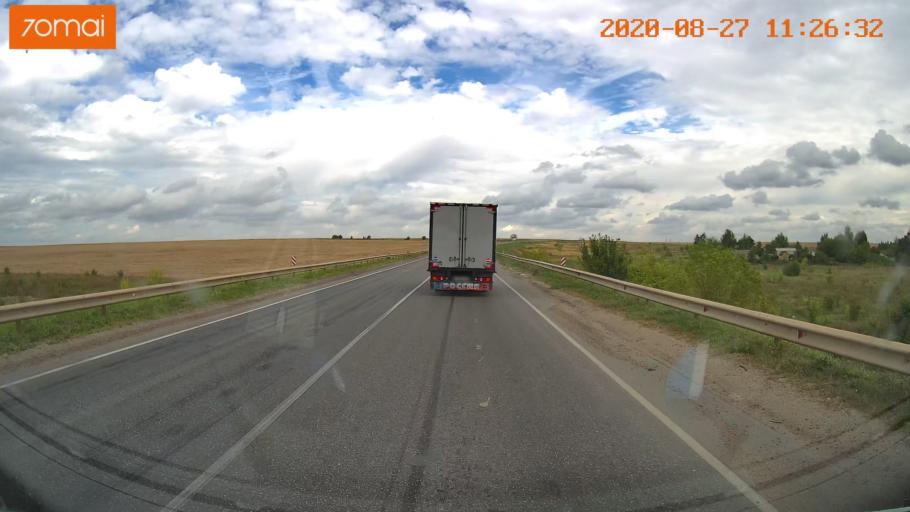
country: RU
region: Rjazan
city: Mikhaylov
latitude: 54.2411
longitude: 38.9840
